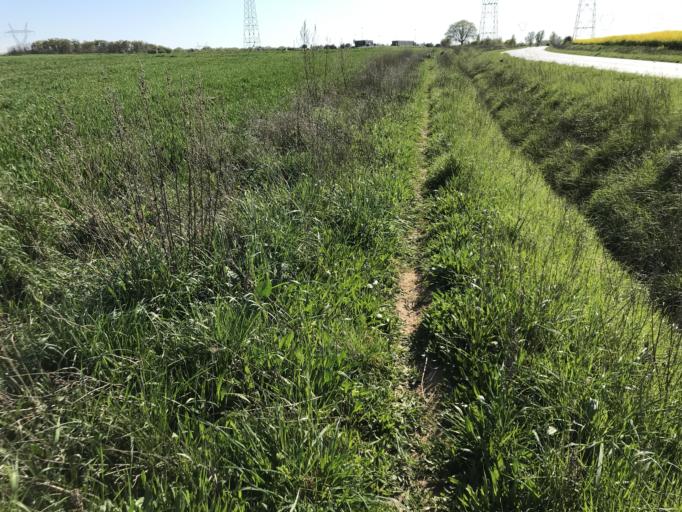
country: FR
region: Ile-de-France
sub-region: Departement de l'Essonne
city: Villejust
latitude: 48.6679
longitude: 2.2209
